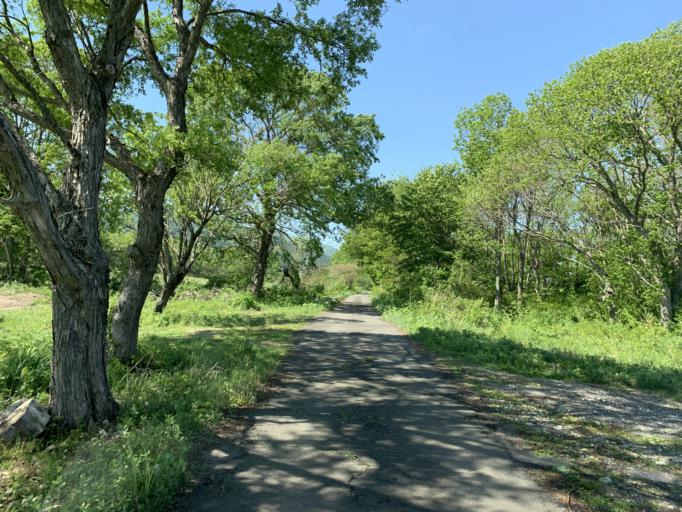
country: JP
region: Iwate
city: Shizukuishi
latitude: 39.5511
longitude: 140.8211
